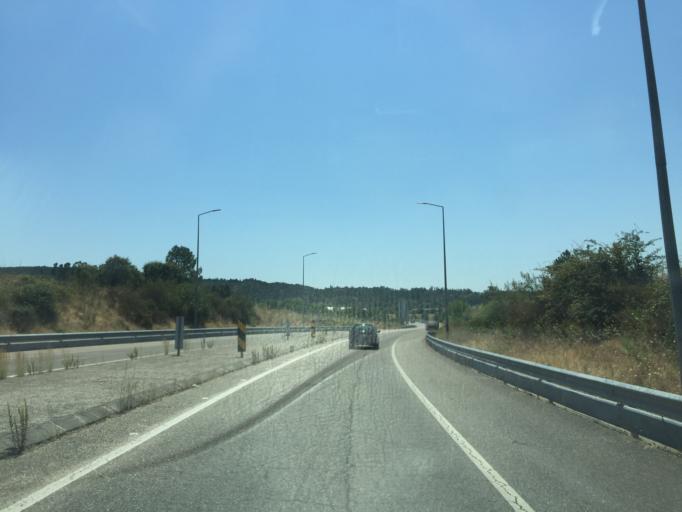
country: PT
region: Santarem
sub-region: Tomar
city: Tomar
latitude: 39.5940
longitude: -8.3620
